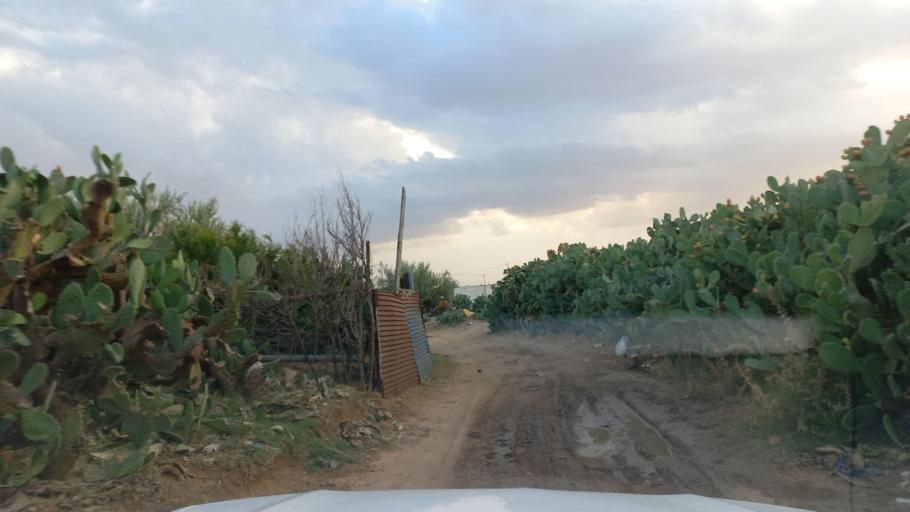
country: TN
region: Al Qasrayn
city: Kasserine
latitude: 35.2703
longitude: 9.0653
